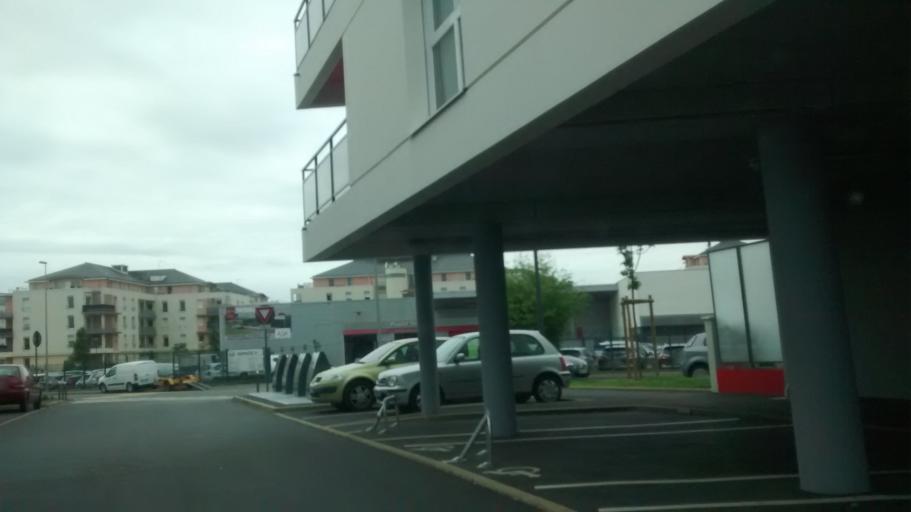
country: FR
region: Brittany
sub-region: Departement d'Ille-et-Vilaine
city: Cesson-Sevigne
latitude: 48.1137
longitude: -1.6174
